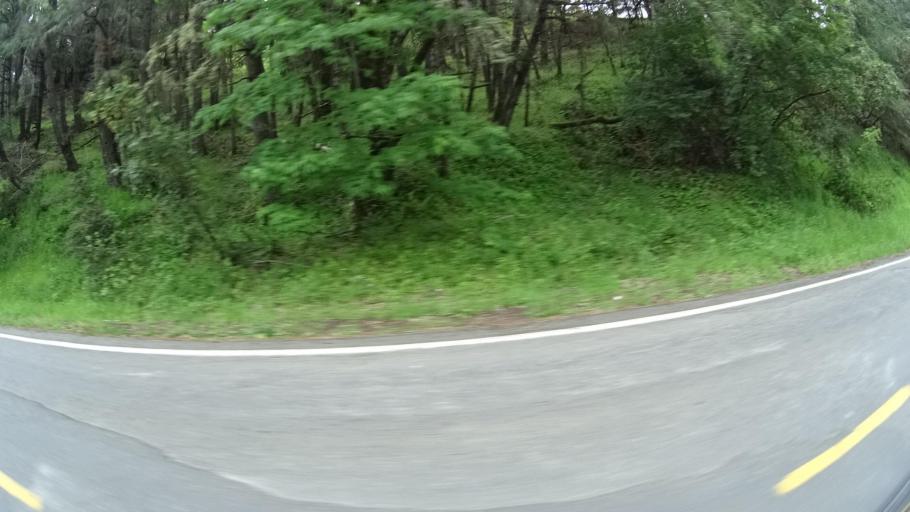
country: US
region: California
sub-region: Humboldt County
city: Redway
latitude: 40.1114
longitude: -123.7766
